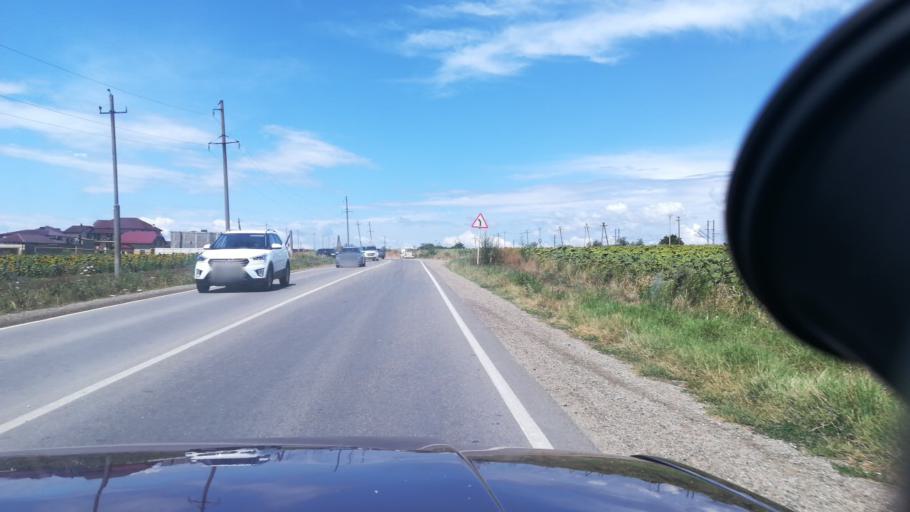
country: RU
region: Krasnodarskiy
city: Tsibanobalka
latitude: 44.9612
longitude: 37.3038
